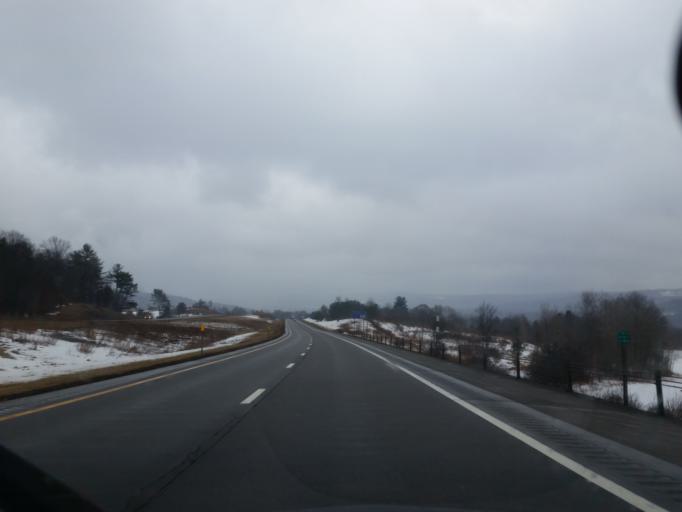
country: US
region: New York
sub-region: Chenango County
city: Lakeview
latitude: 42.3537
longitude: -75.9907
